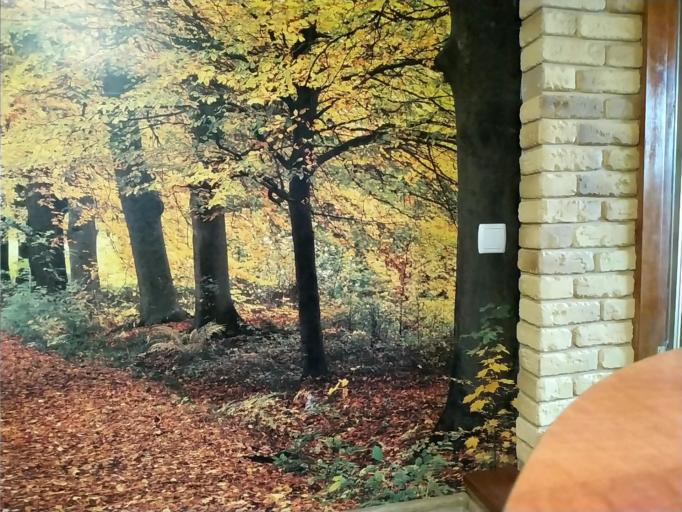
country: RU
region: Leningrad
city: Tolmachevo
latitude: 58.9338
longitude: 29.7037
